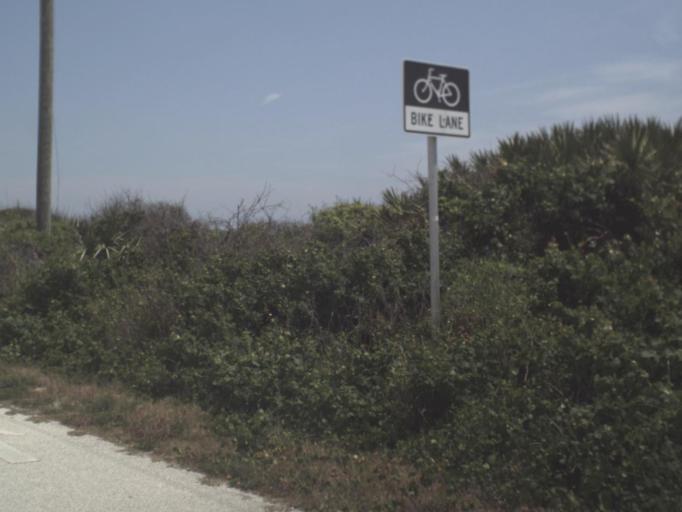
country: US
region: Florida
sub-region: Saint Johns County
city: Villano Beach
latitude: 30.0232
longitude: -81.3235
